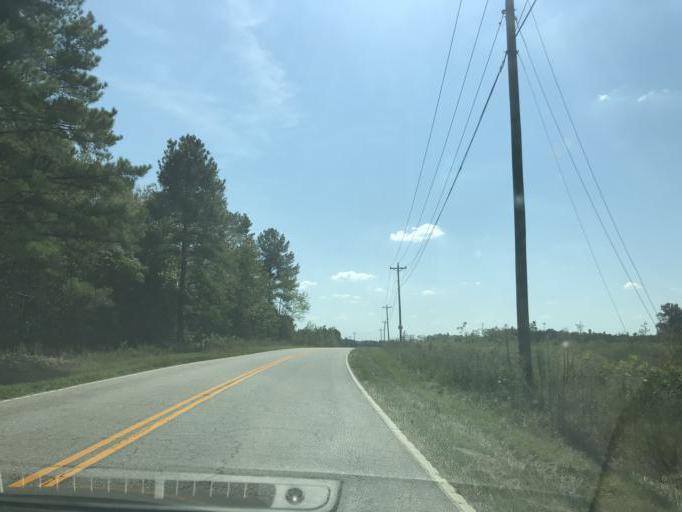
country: US
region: South Carolina
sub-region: Cherokee County
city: Gaffney
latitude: 35.0979
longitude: -81.7093
